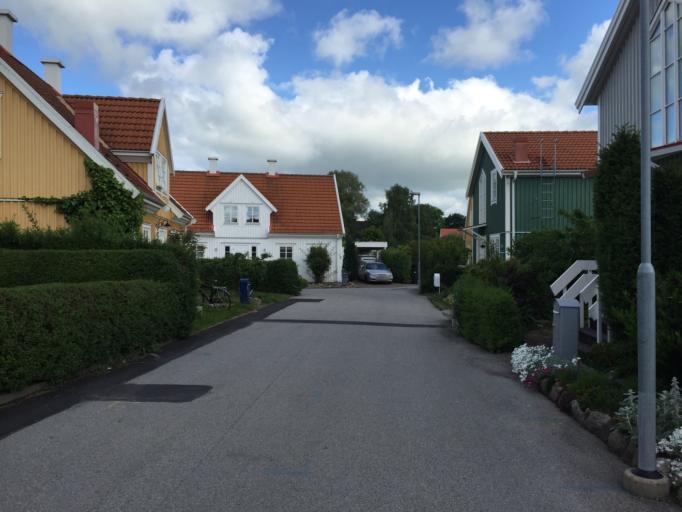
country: SE
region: Skane
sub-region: Lunds Kommun
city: Lund
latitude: 55.7287
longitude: 13.1889
